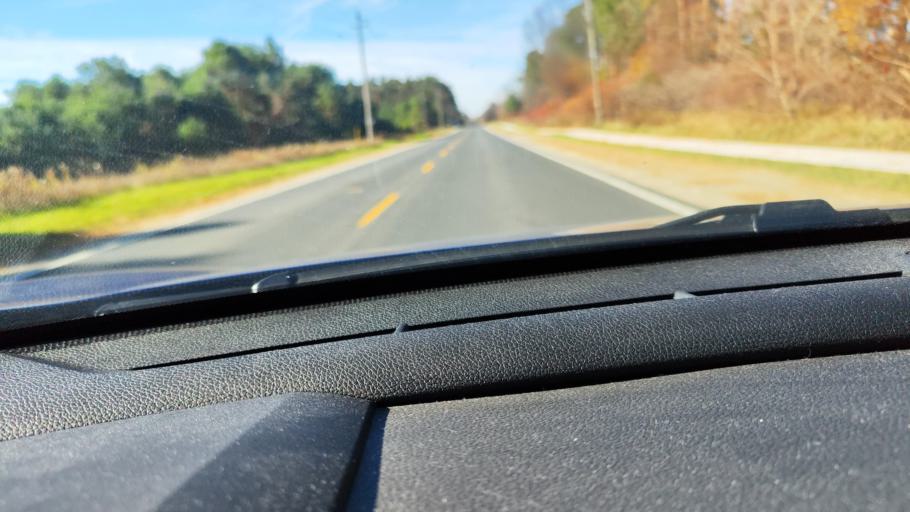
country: CA
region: Ontario
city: Angus
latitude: 44.3554
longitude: -79.9852
